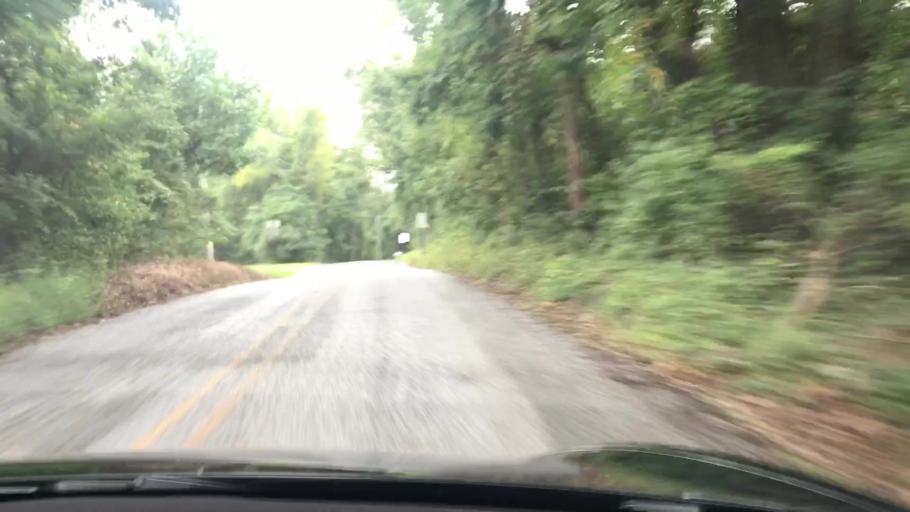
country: US
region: Pennsylvania
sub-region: York County
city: Dillsburg
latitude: 40.1116
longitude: -76.9696
